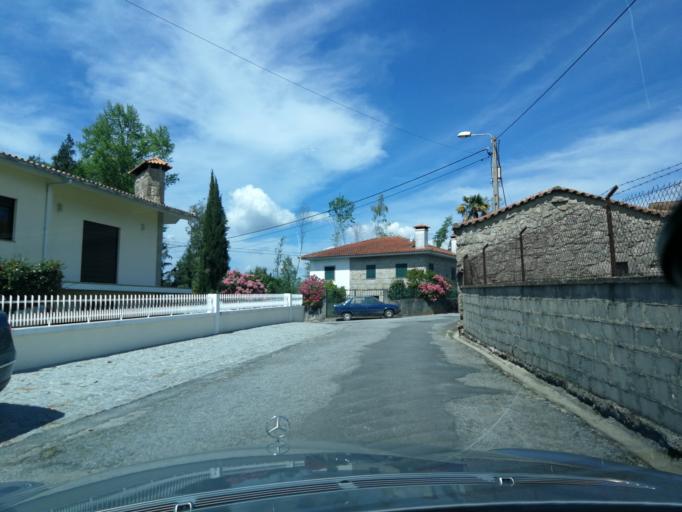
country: PT
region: Braga
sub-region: Vila Nova de Famalicao
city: Vila Nova de Famalicao
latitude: 41.4300
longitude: -8.5280
